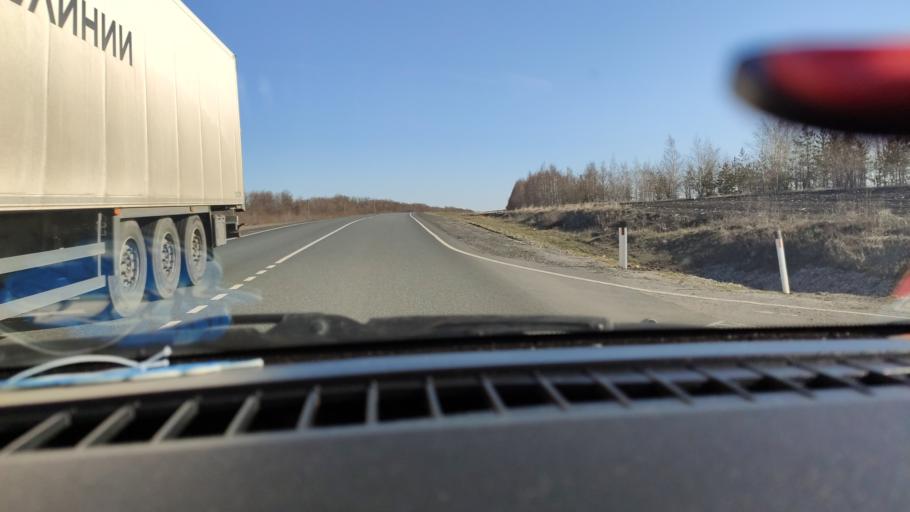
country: RU
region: Samara
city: Syzran'
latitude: 52.9768
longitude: 48.3102
